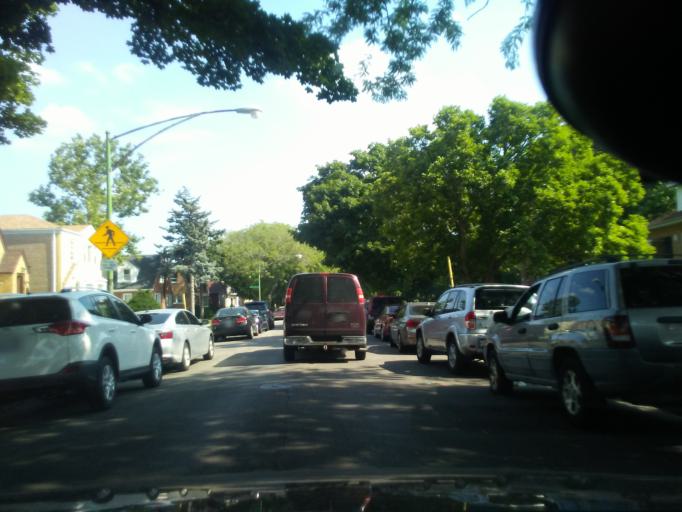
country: US
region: Illinois
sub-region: Cook County
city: Elmwood Park
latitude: 41.9344
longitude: -87.7688
